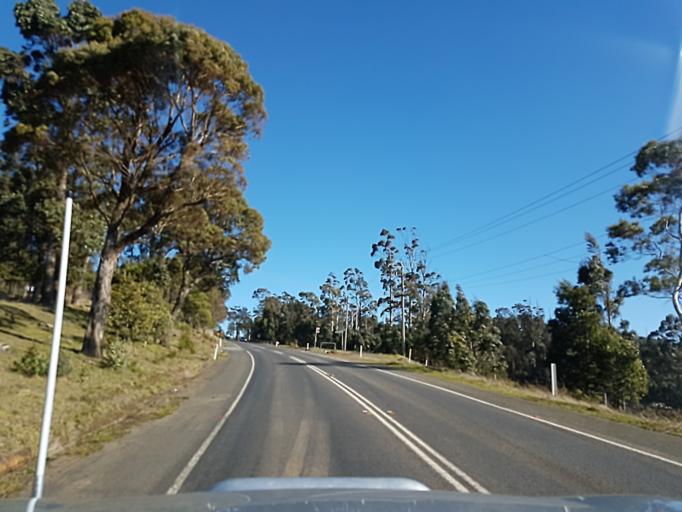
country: AU
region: Victoria
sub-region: Nillumbik
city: Saint Andrews
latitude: -37.5227
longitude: 145.3259
